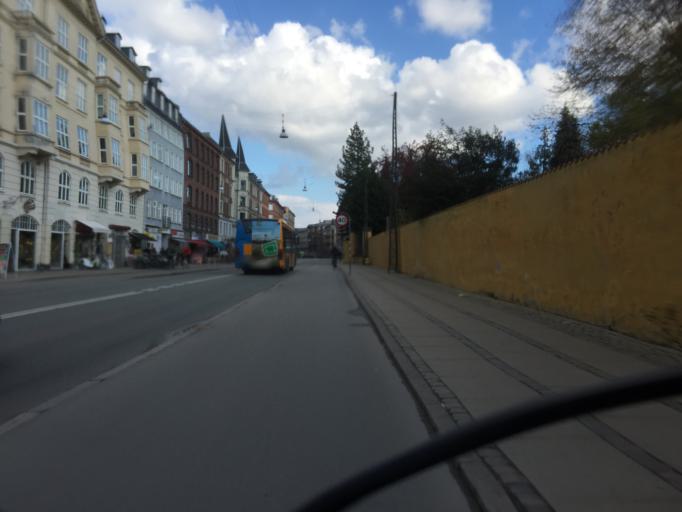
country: DK
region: Capital Region
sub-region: Kobenhavn
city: Copenhagen
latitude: 55.6916
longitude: 12.5530
